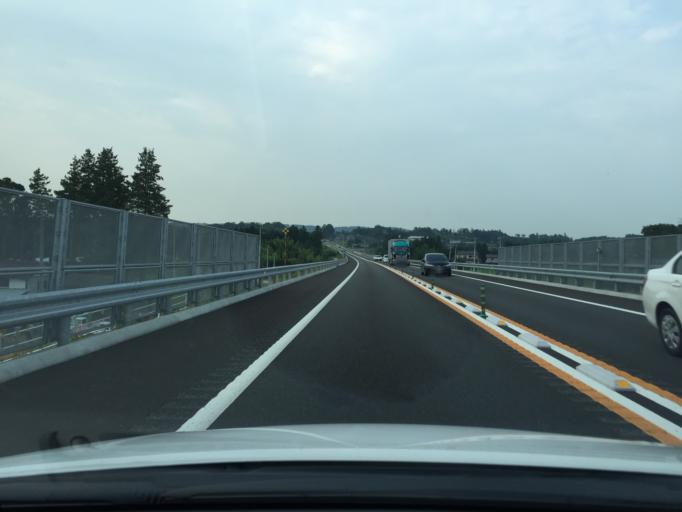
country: JP
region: Fukushima
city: Namie
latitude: 37.5555
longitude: 140.9452
